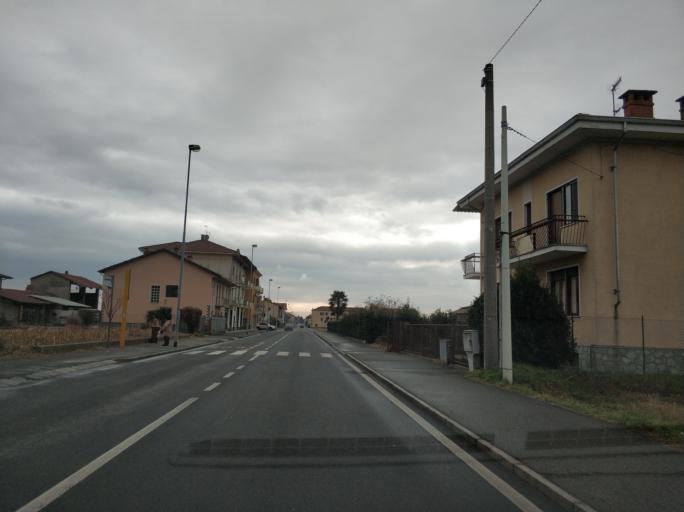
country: IT
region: Piedmont
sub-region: Provincia di Torino
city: Banchette
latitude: 45.4411
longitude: 7.8777
